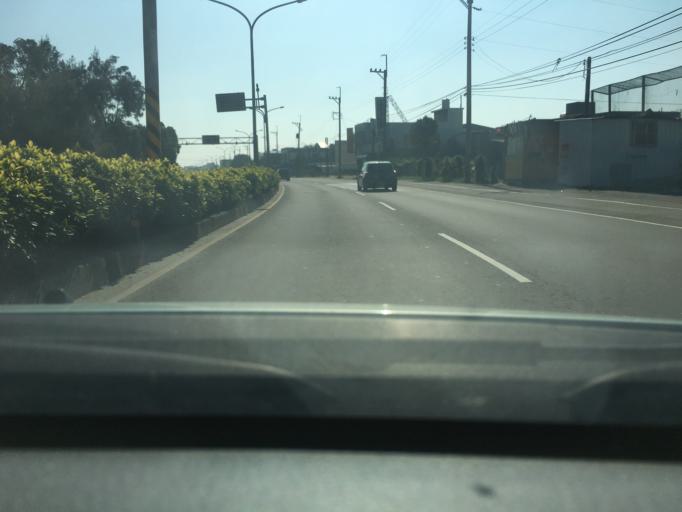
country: TW
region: Taiwan
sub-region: Hsinchu
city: Hsinchu
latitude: 24.8183
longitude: 120.9240
